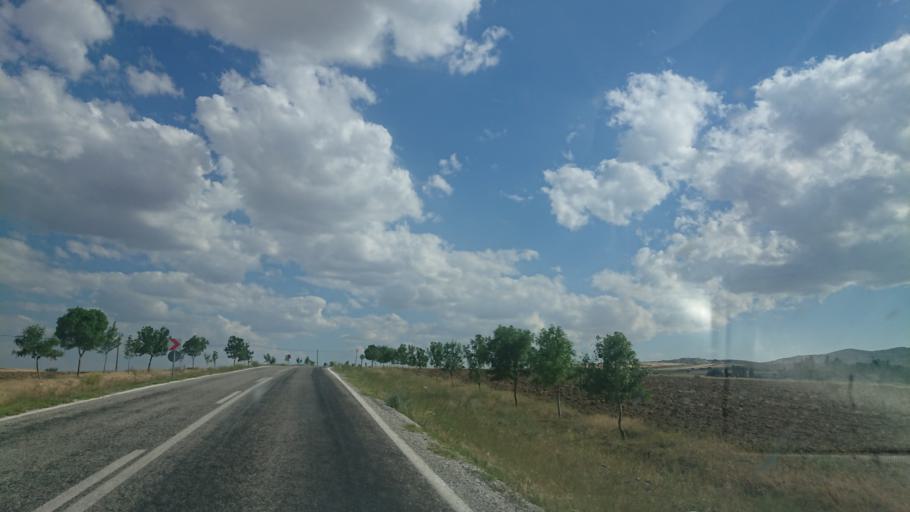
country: TR
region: Aksaray
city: Sariyahsi
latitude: 38.9503
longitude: 33.8389
